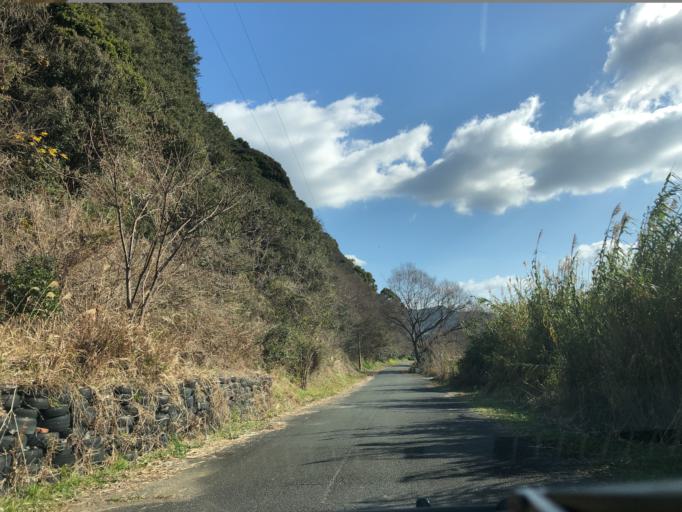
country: JP
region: Kochi
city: Sukumo
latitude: 32.9121
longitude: 132.6980
